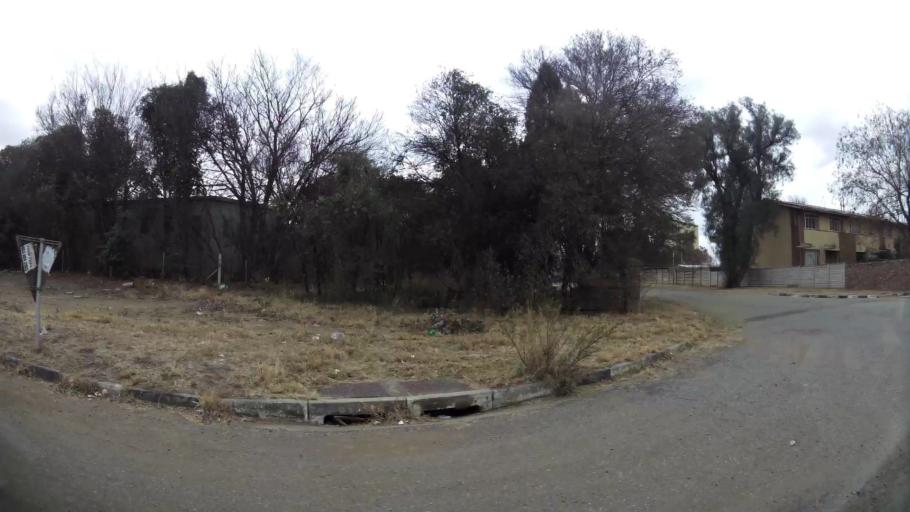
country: ZA
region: Orange Free State
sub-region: Fezile Dabi District Municipality
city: Kroonstad
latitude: -27.6593
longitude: 27.2375
